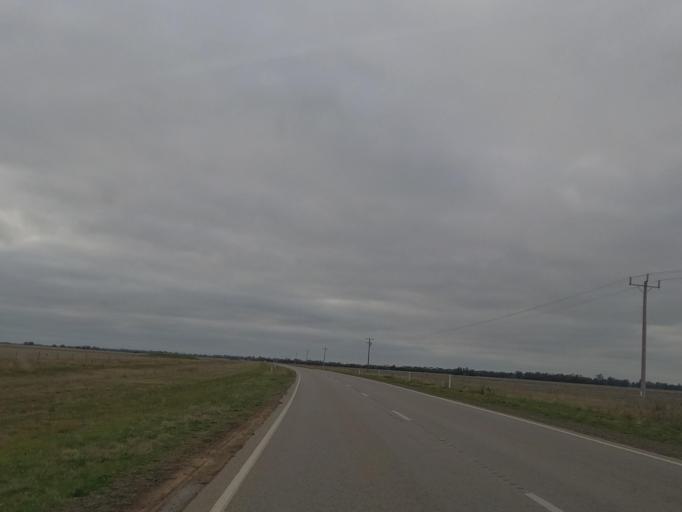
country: AU
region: Victoria
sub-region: Greater Bendigo
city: Long Gully
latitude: -36.4790
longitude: 143.9619
